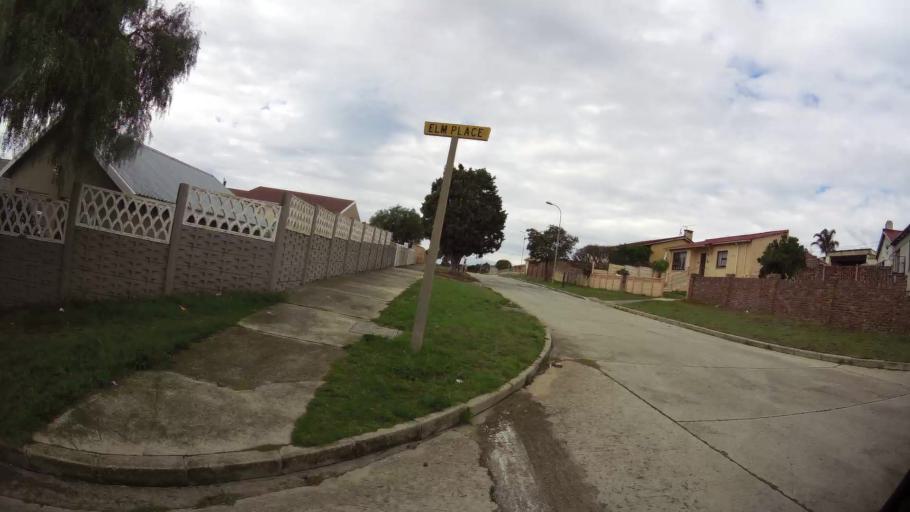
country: ZA
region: Eastern Cape
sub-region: Nelson Mandela Bay Metropolitan Municipality
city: Port Elizabeth
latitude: -33.9391
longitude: 25.5849
